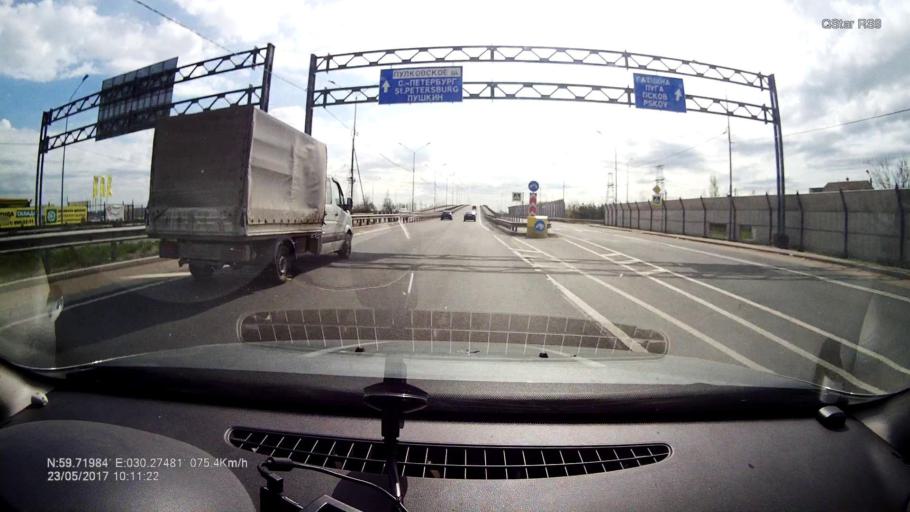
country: RU
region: St.-Petersburg
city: Aleksandrovskaya
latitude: 59.7198
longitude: 30.2750
